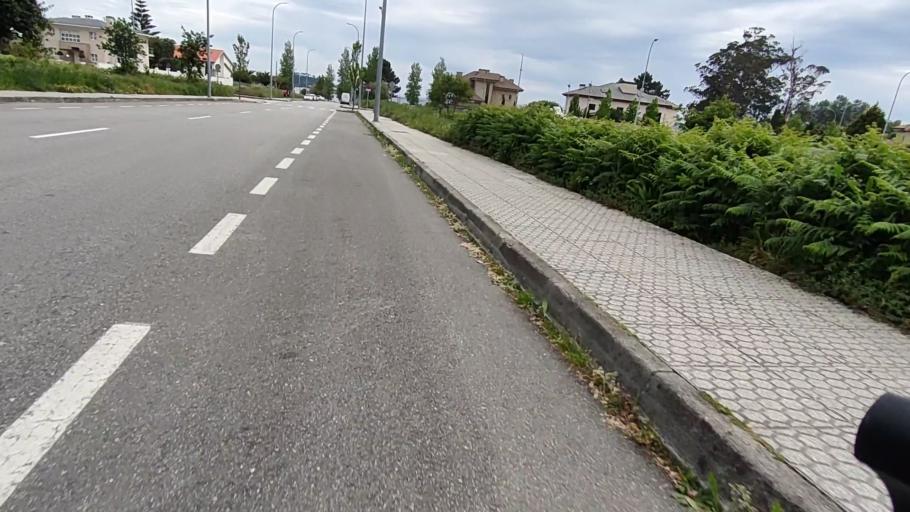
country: ES
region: Galicia
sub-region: Provincia da Coruna
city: Boiro
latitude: 42.6425
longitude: -8.8868
